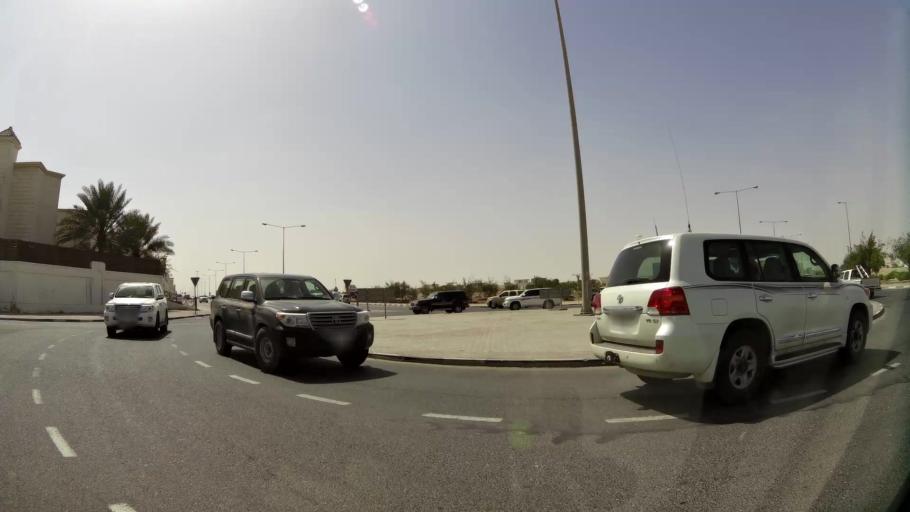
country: QA
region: Baladiyat Umm Salal
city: Umm Salal Muhammad
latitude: 25.3751
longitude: 51.4318
